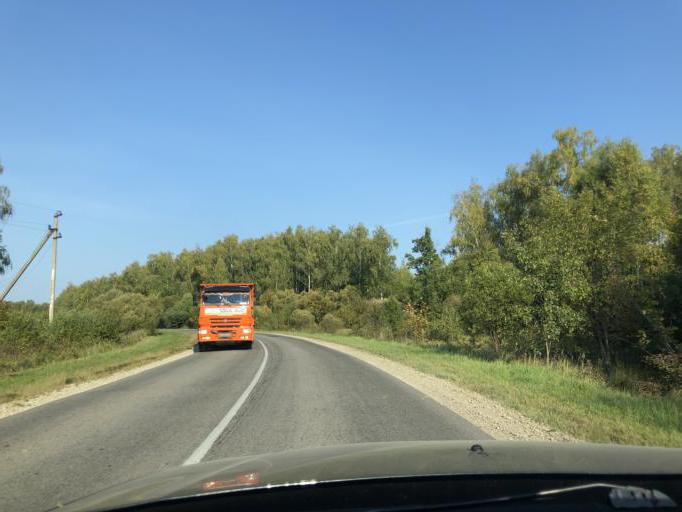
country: RU
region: Tula
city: Leninskiy
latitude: 54.3309
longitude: 37.3913
